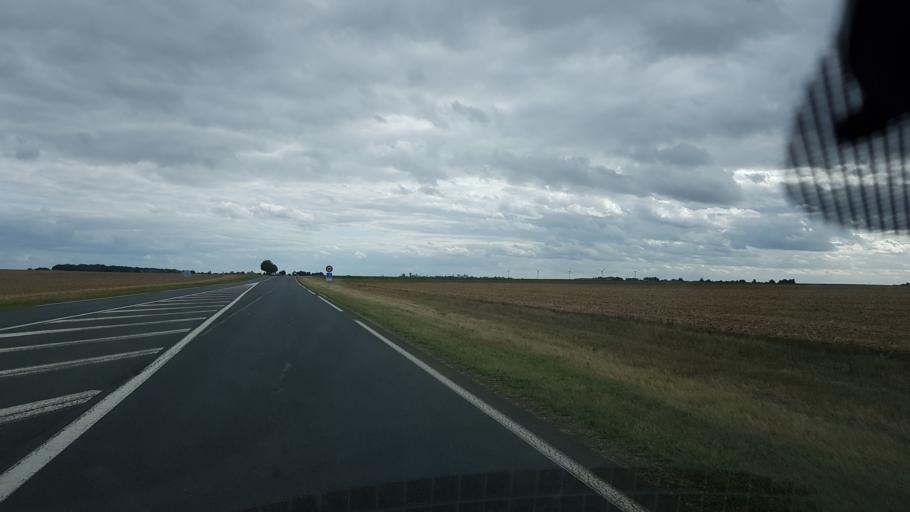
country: FR
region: Centre
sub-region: Departement du Loiret
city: Sermaises
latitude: 48.2446
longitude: 2.2202
